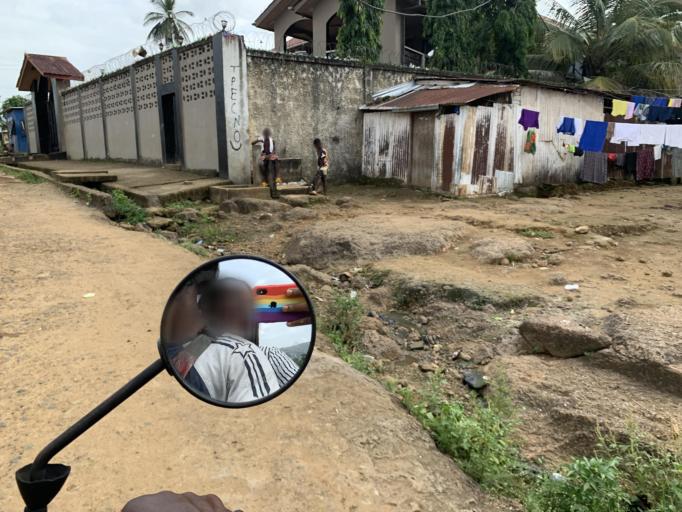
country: SL
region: Western Area
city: Hastings
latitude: 8.3907
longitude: -13.1514
